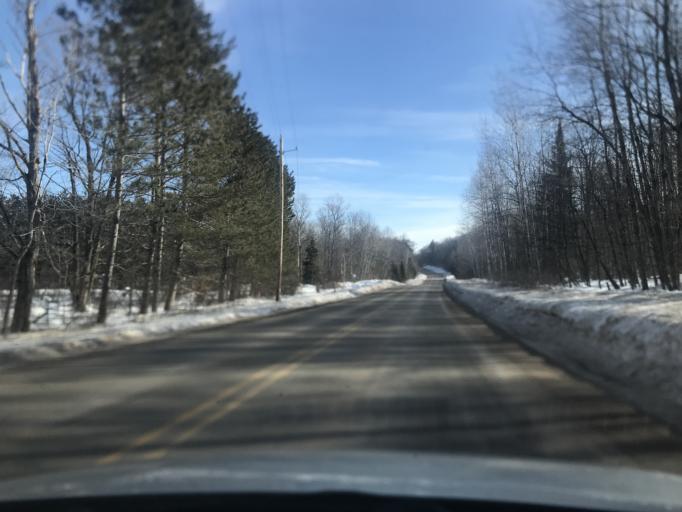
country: US
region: Michigan
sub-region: Dickinson County
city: Kingsford
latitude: 45.4191
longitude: -88.4076
